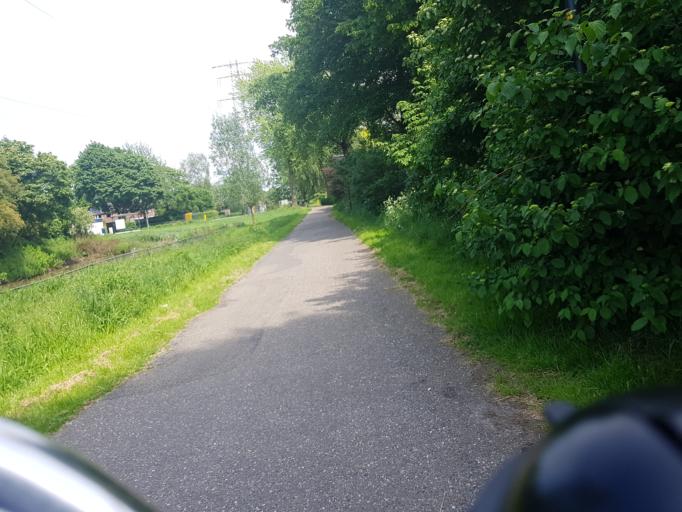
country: NL
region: Gelderland
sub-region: Gemeente Apeldoorn
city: Apeldoorn
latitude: 52.1868
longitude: 5.9959
